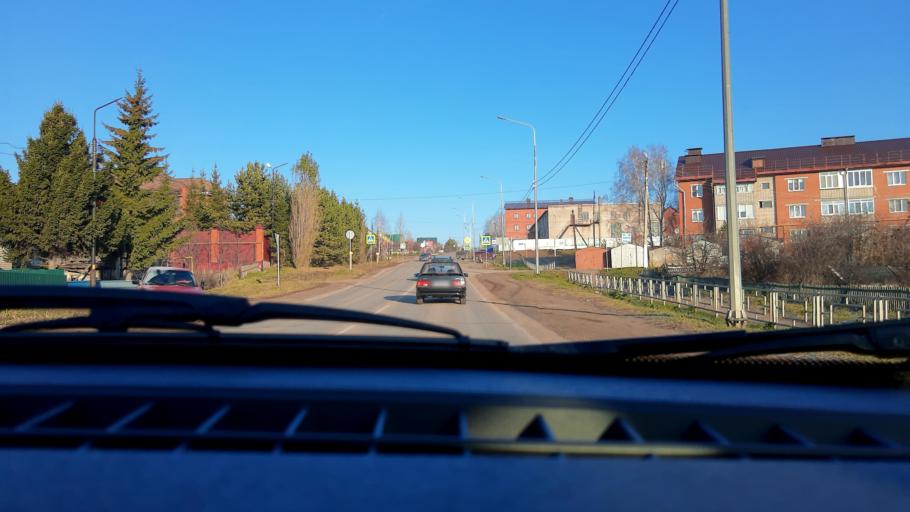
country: RU
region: Bashkortostan
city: Mikhaylovka
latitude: 54.8065
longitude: 55.8901
